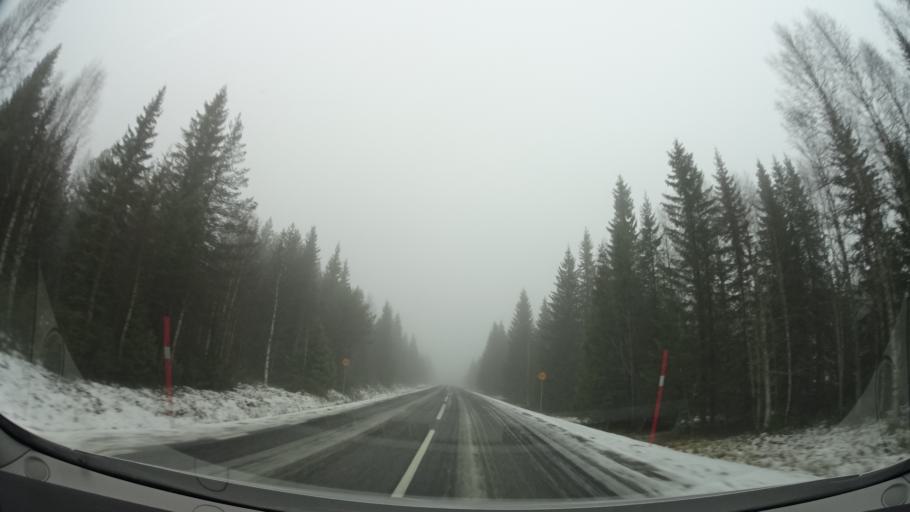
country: SE
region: Vaesterbotten
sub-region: Asele Kommun
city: Insjon
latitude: 64.3579
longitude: 17.9183
